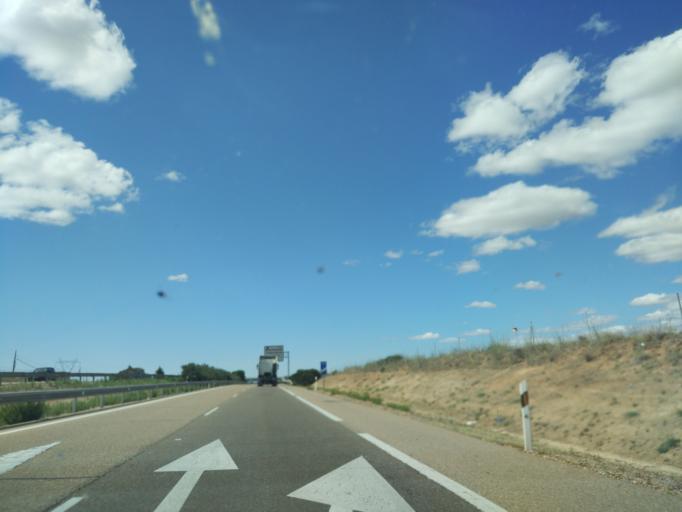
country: ES
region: Castille and Leon
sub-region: Provincia de Valladolid
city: Rueda
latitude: 41.4387
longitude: -4.9746
